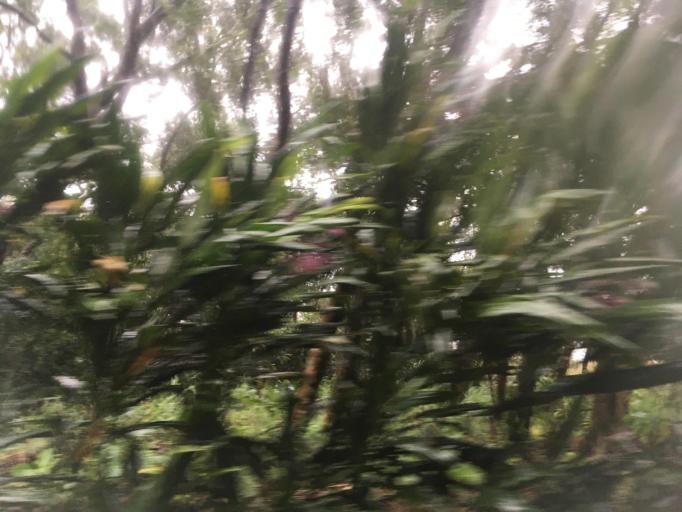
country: TW
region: Taiwan
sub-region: Keelung
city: Keelung
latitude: 25.0670
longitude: 121.9016
